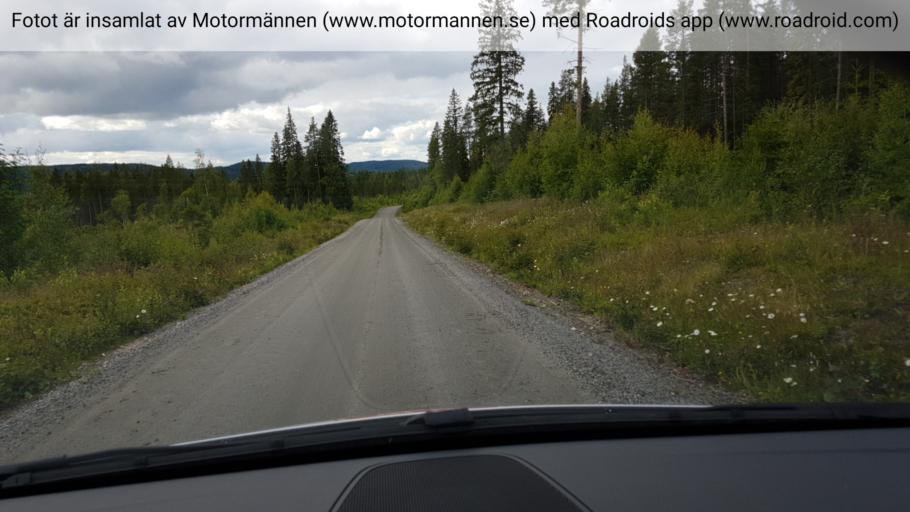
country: SE
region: Vaesterbotten
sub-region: Dorotea Kommun
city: Dorotea
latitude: 63.9332
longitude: 16.1036
